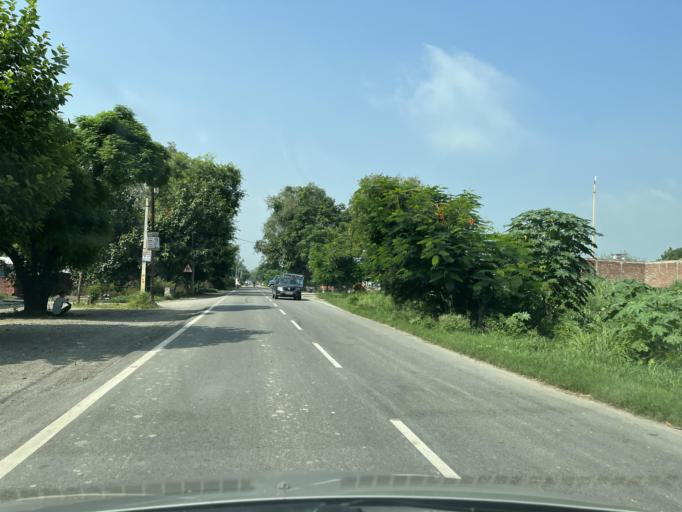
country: IN
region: Uttarakhand
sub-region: Udham Singh Nagar
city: Bazpur
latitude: 29.1838
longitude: 79.1825
